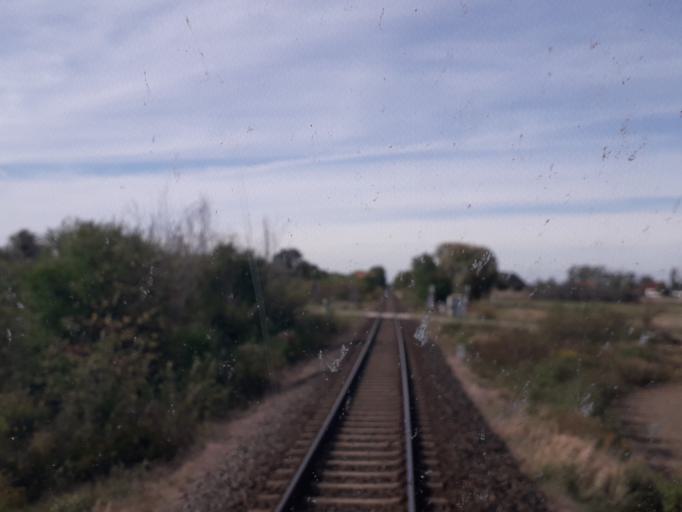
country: DE
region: Brandenburg
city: Velten
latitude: 52.7192
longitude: 13.1206
